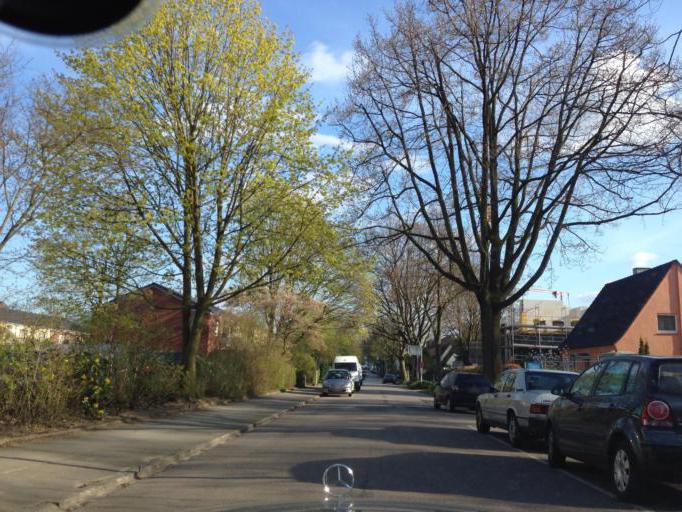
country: DE
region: Hamburg
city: Marienthal
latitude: 53.5851
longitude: 10.0861
